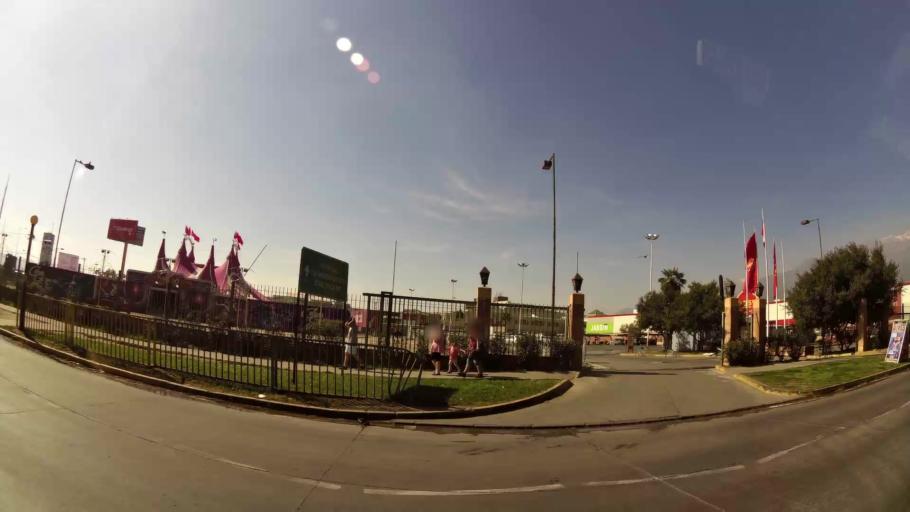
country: CL
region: Santiago Metropolitan
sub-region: Provincia de Santiago
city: Villa Presidente Frei, Nunoa, Santiago, Chile
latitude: -33.4898
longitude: -70.5786
